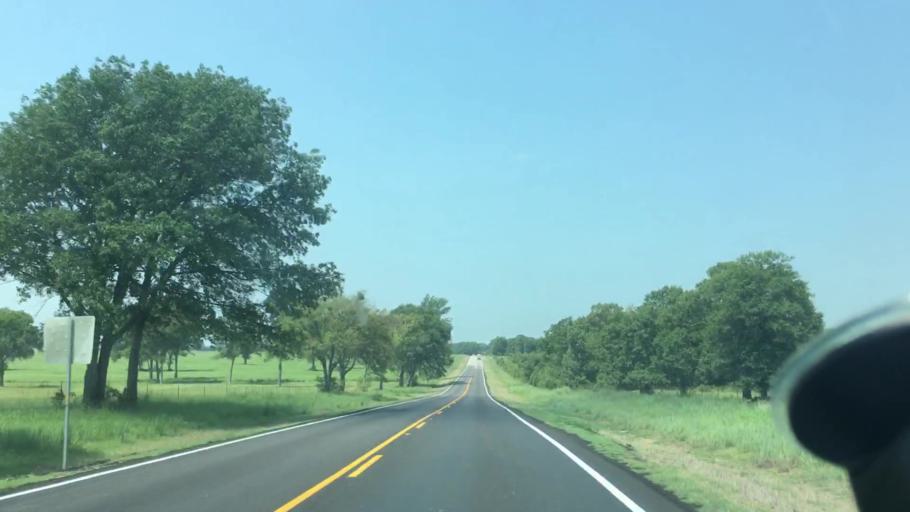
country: US
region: Oklahoma
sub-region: Atoka County
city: Atoka
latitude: 34.2785
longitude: -95.9377
